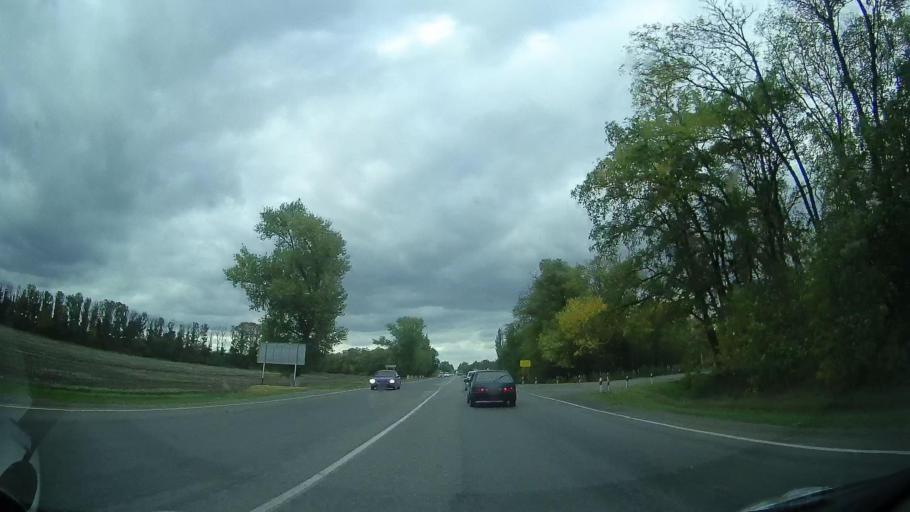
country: RU
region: Rostov
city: Zernograd
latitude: 46.8302
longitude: 40.2407
